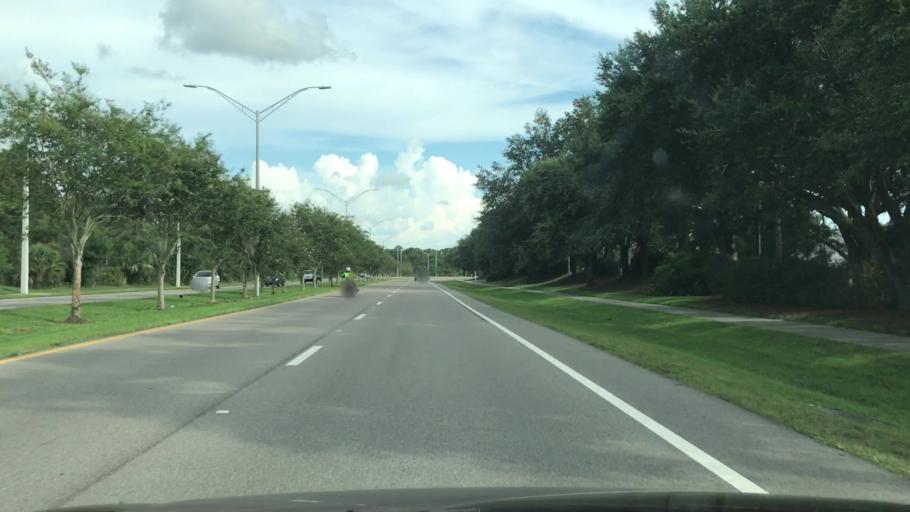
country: US
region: Florida
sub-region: Sarasota County
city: Venice Gardens
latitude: 27.0880
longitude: -82.3889
